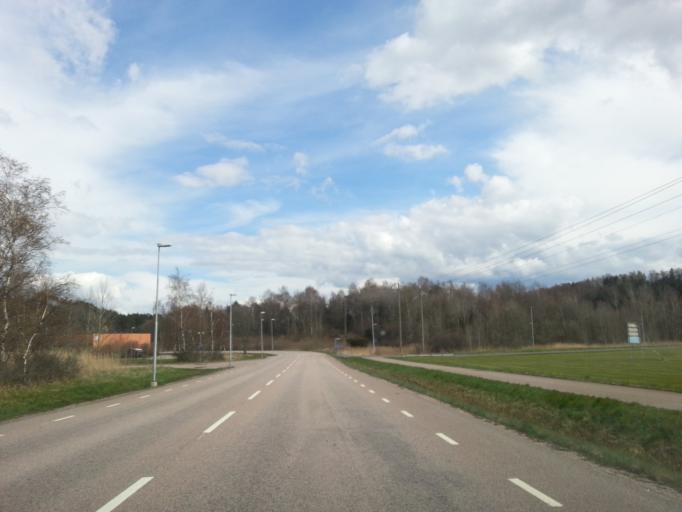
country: SE
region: Vaestra Goetaland
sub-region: Kungalvs Kommun
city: Kungalv
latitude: 57.8713
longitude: 11.9373
